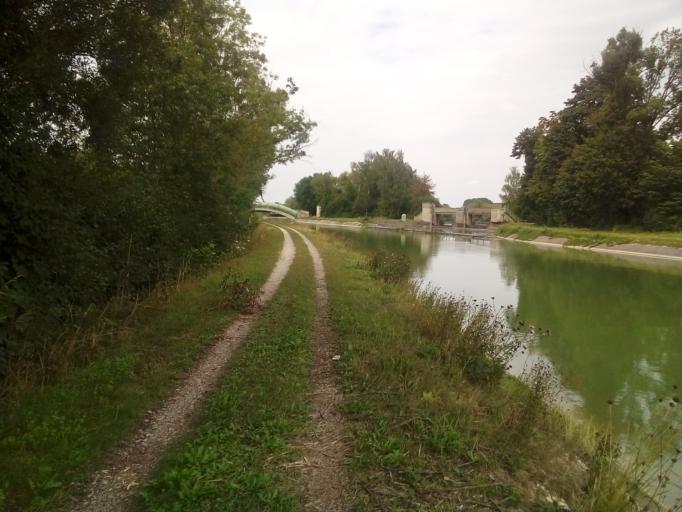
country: DE
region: Bavaria
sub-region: Upper Bavaria
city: Unterfoehring
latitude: 48.2024
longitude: 11.6661
